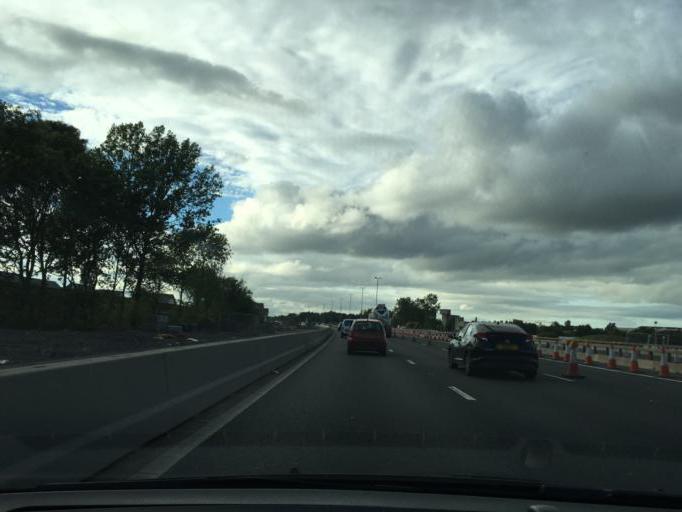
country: GB
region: Scotland
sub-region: South Lanarkshire
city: Bothwell
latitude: 55.8171
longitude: -4.0660
